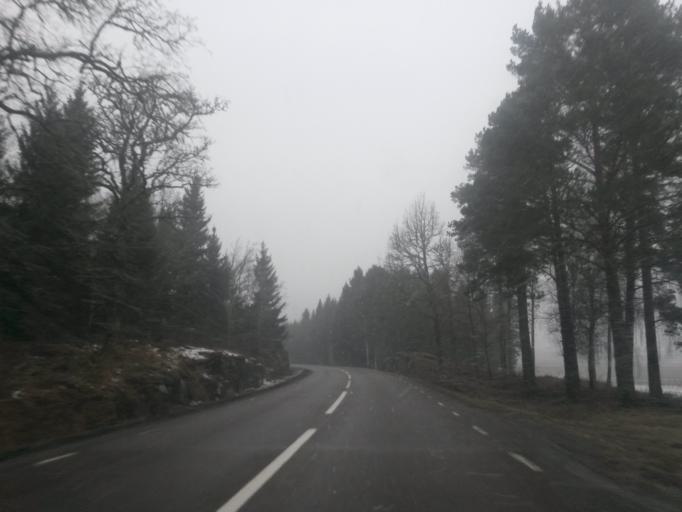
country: SE
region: Vaestra Goetaland
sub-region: Alingsas Kommun
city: Sollebrunn
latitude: 58.2133
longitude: 12.4327
